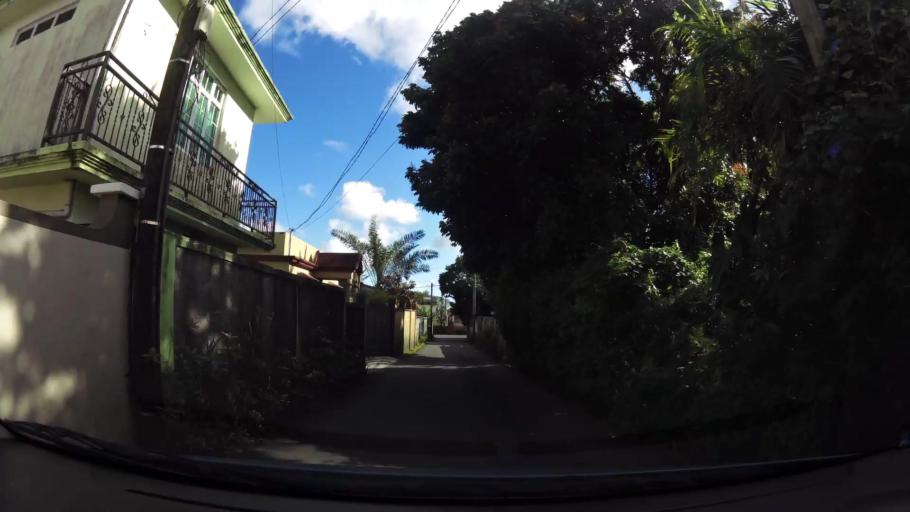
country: MU
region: Plaines Wilhems
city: Curepipe
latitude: -20.3005
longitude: 57.5176
